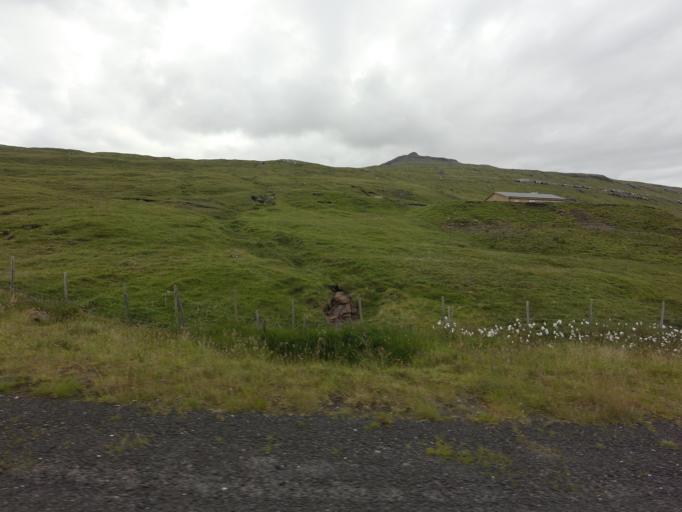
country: FO
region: Eysturoy
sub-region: Eidi
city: Eidi
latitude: 62.2133
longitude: -6.9969
